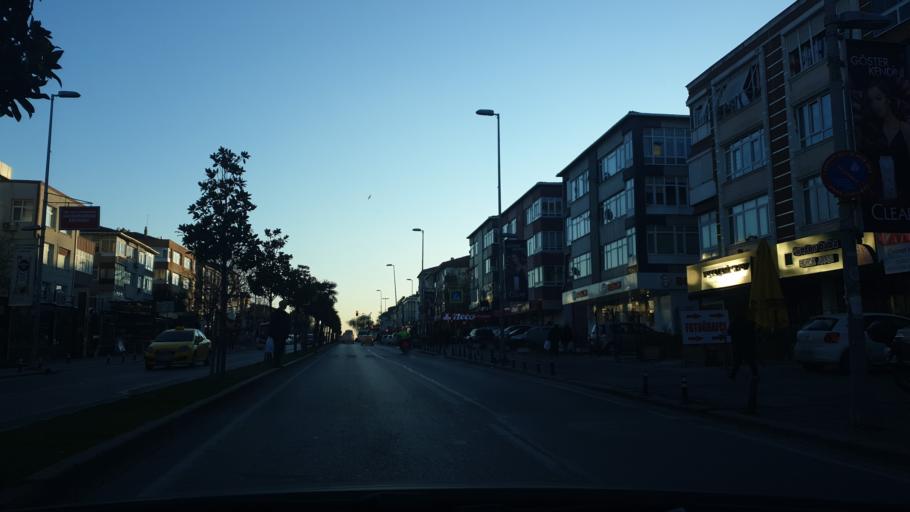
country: TR
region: Istanbul
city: Bahcelievler
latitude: 41.0017
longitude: 28.8630
